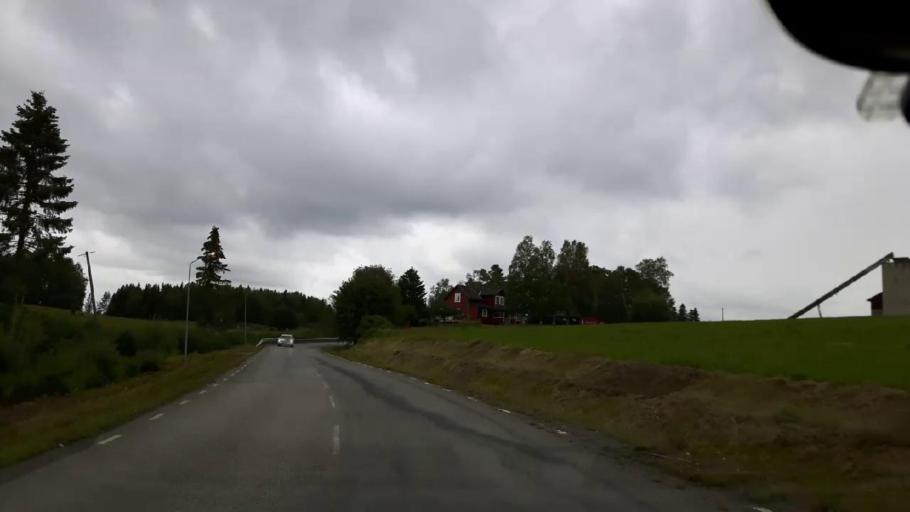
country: SE
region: Jaemtland
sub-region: OEstersunds Kommun
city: Ostersund
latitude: 63.0019
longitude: 14.5832
